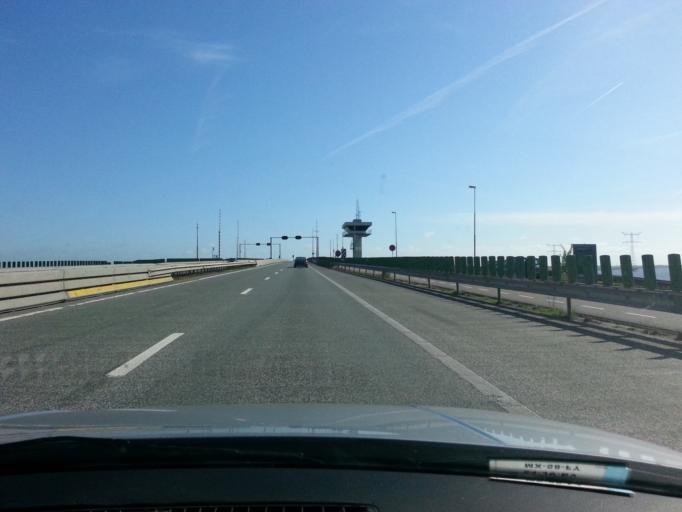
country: NL
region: Flevoland
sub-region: Gemeente Urk
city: Urk
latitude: 52.6096
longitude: 5.6404
